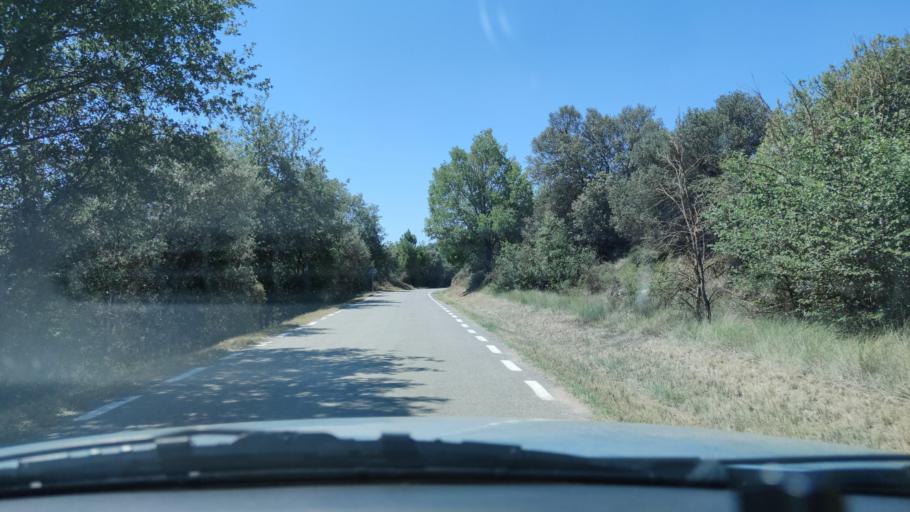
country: ES
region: Catalonia
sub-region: Provincia de Lleida
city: Tora de Riubregos
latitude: 41.8407
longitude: 1.4227
